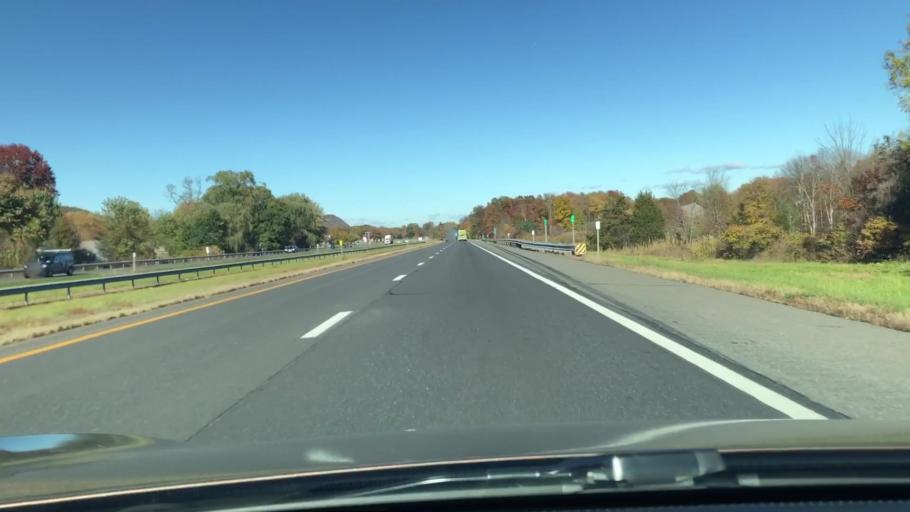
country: US
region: New York
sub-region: Ulster County
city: Lake Katrine
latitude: 42.0093
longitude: -74.0004
